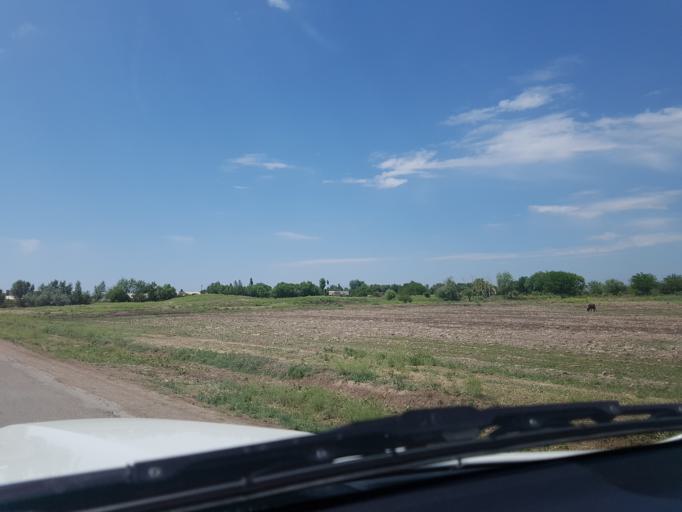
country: TM
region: Dasoguz
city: Koeneuergench
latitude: 42.3187
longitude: 59.1396
